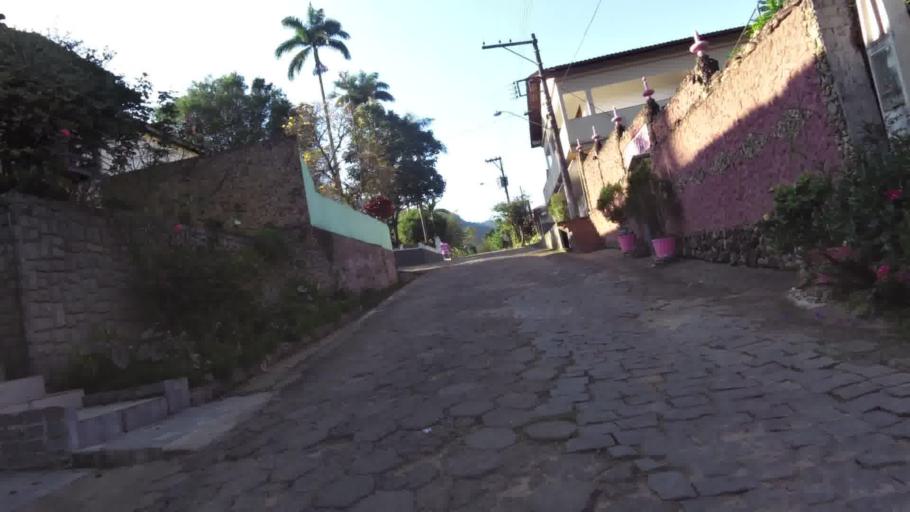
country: BR
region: Espirito Santo
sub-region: Alfredo Chaves
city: Alfredo Chaves
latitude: -20.5805
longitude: -40.6977
